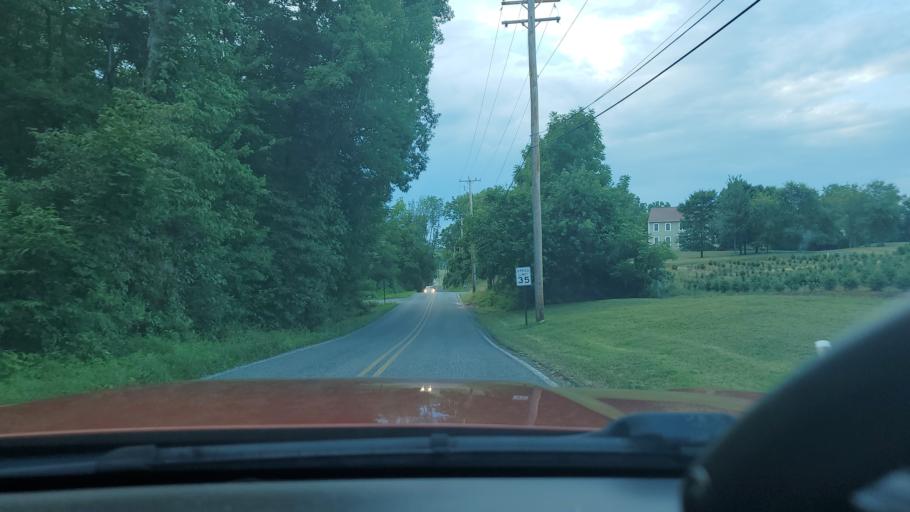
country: US
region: Pennsylvania
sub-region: Montgomery County
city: Limerick
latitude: 40.2430
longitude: -75.5213
